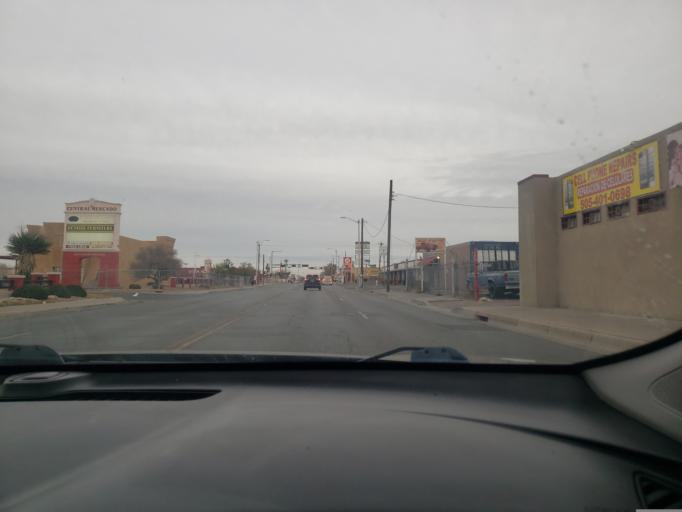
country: US
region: New Mexico
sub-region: Bernalillo County
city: Albuquerque
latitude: 35.0750
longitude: -106.5775
